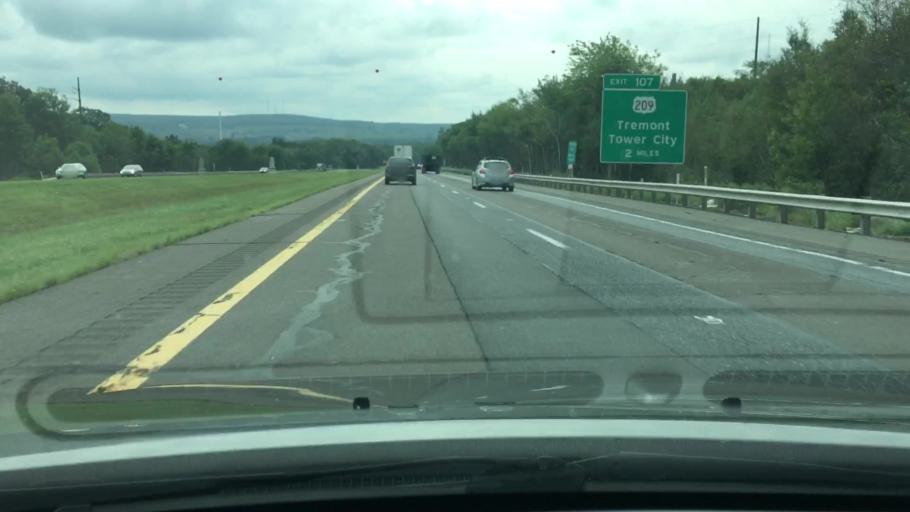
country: US
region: Pennsylvania
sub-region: Schuylkill County
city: Tremont
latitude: 40.6399
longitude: -76.4326
